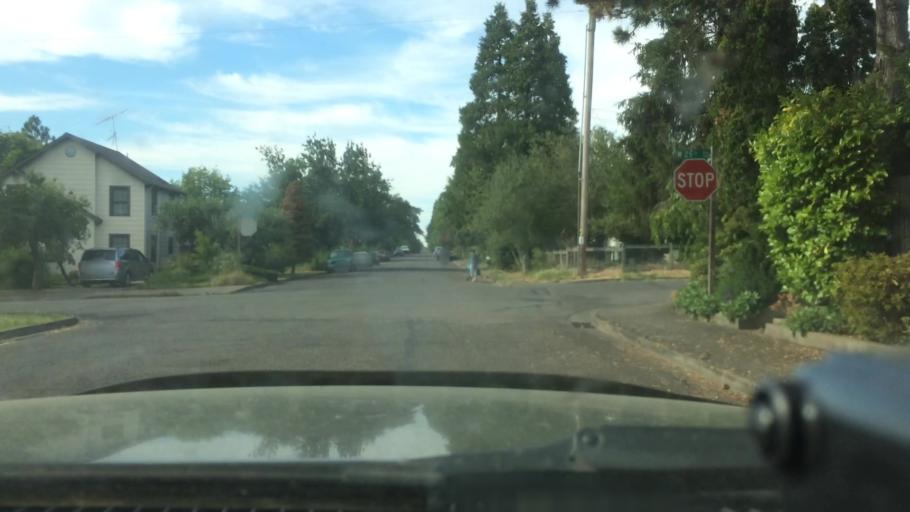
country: US
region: Oregon
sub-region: Lane County
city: Eugene
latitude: 44.0312
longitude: -123.1041
